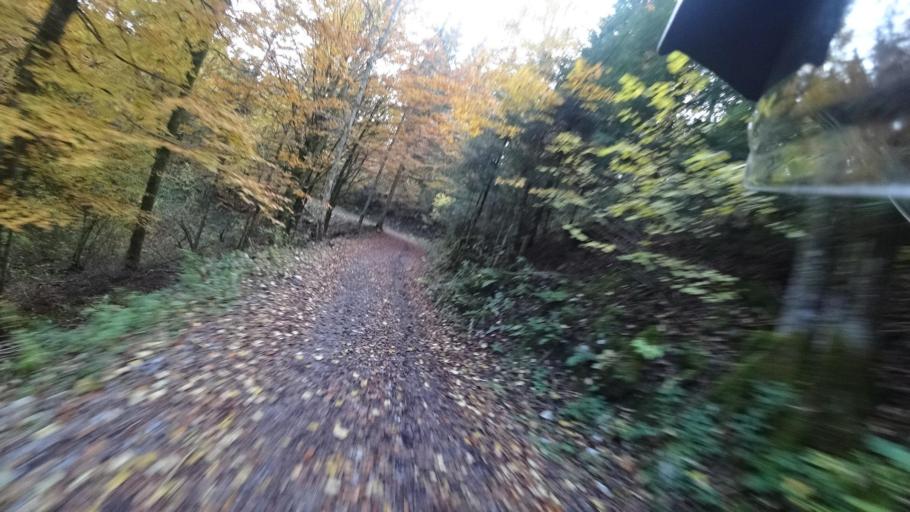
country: HR
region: Primorsko-Goranska
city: Vrbovsko
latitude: 45.2149
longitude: 15.0684
